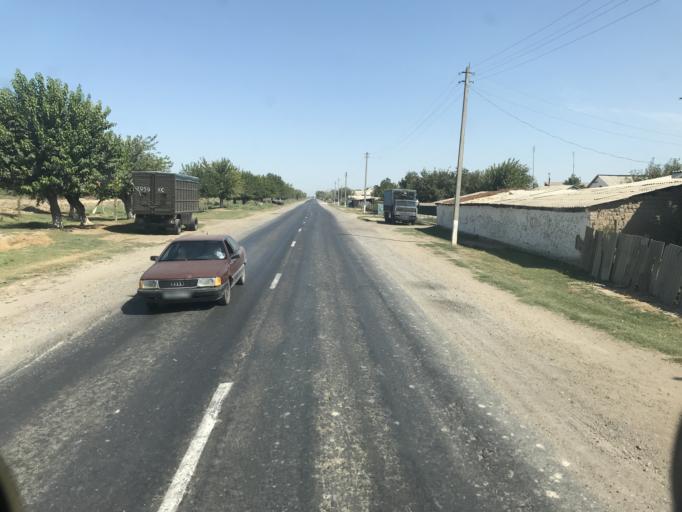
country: KZ
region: Ongtustik Qazaqstan
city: Ilyich
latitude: 40.7612
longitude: 68.5371
